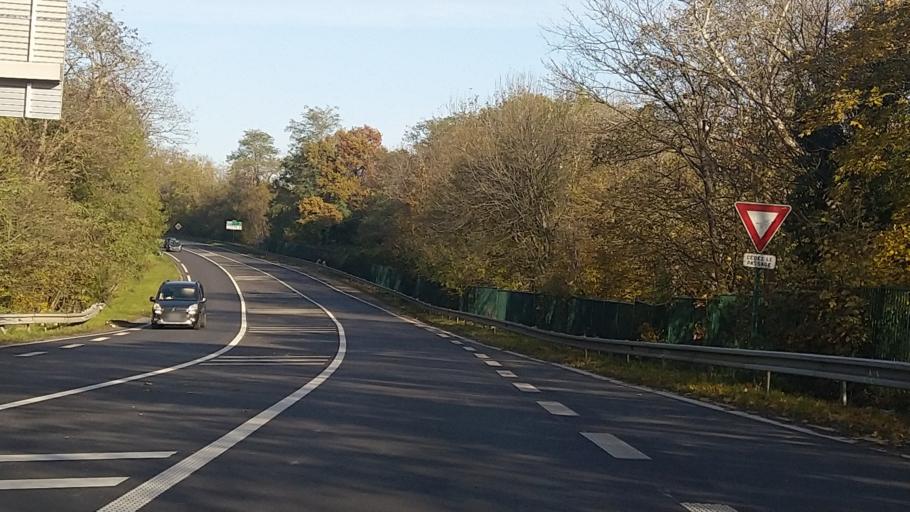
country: FR
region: Ile-de-France
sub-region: Departement du Val-d'Oise
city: Sarcelles
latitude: 48.9875
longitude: 2.3814
